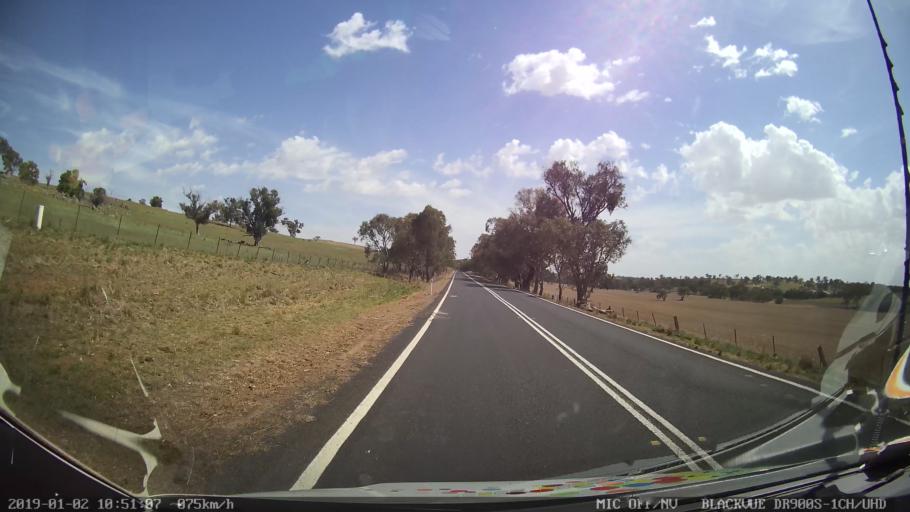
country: AU
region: New South Wales
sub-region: Cootamundra
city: Cootamundra
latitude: -34.7044
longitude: 148.2756
